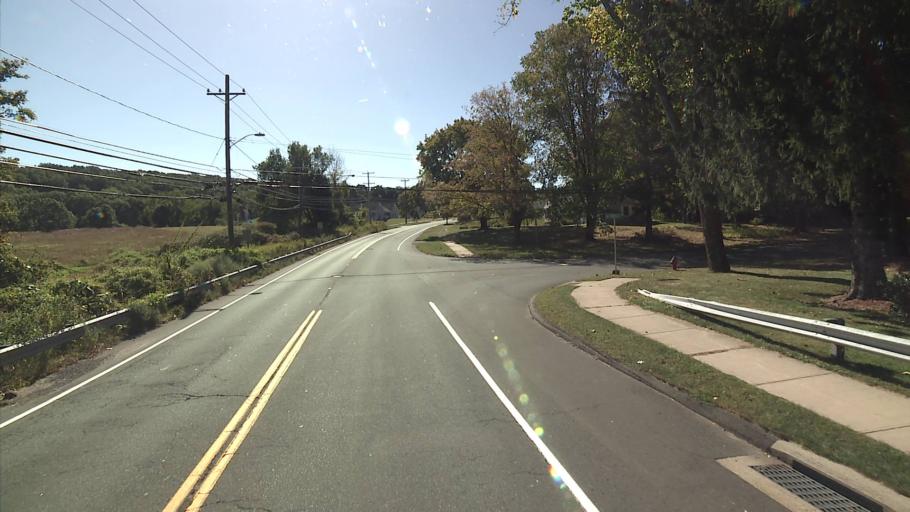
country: US
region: Connecticut
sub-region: Hartford County
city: Bristol
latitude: 41.7009
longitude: -72.9456
